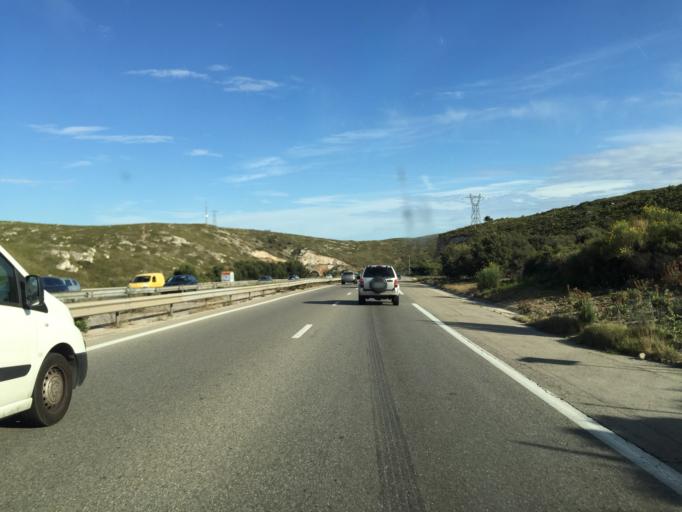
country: FR
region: Provence-Alpes-Cote d'Azur
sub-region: Departement des Bouches-du-Rhone
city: Marseille 16
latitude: 43.3757
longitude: 5.3188
